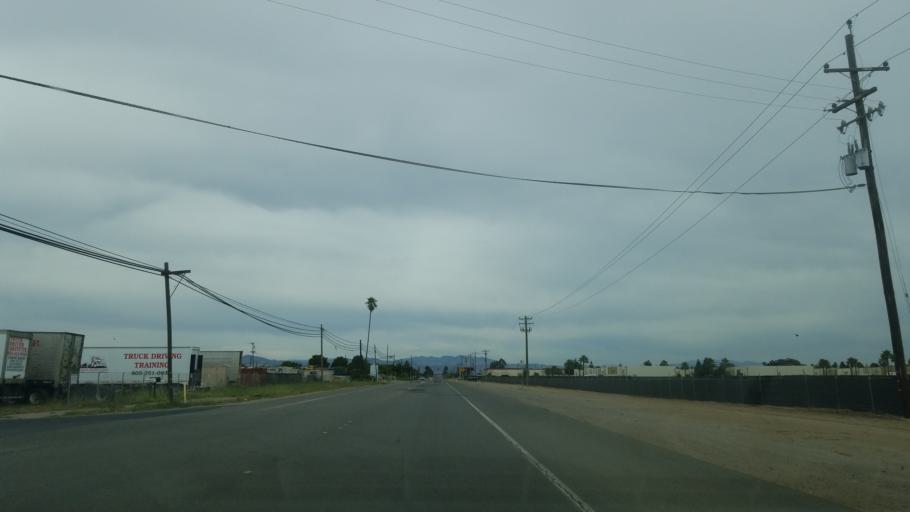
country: US
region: California
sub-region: Santa Barbara County
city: Santa Maria
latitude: 34.9208
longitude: -120.4691
